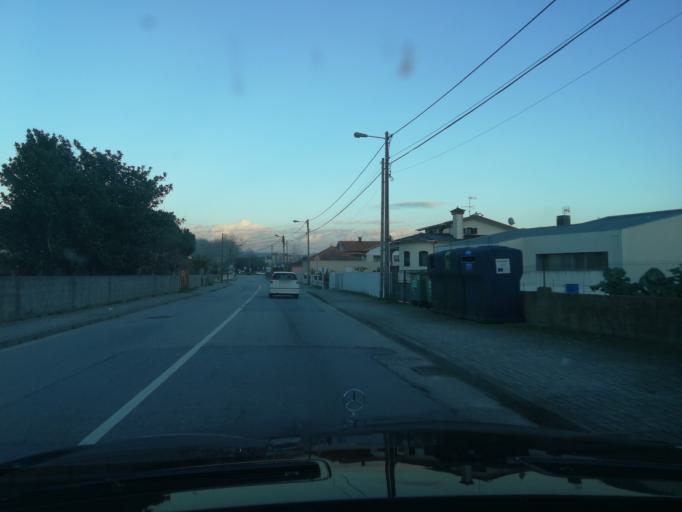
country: PT
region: Aveiro
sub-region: Estarreja
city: Estarreja
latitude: 40.7557
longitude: -8.5837
